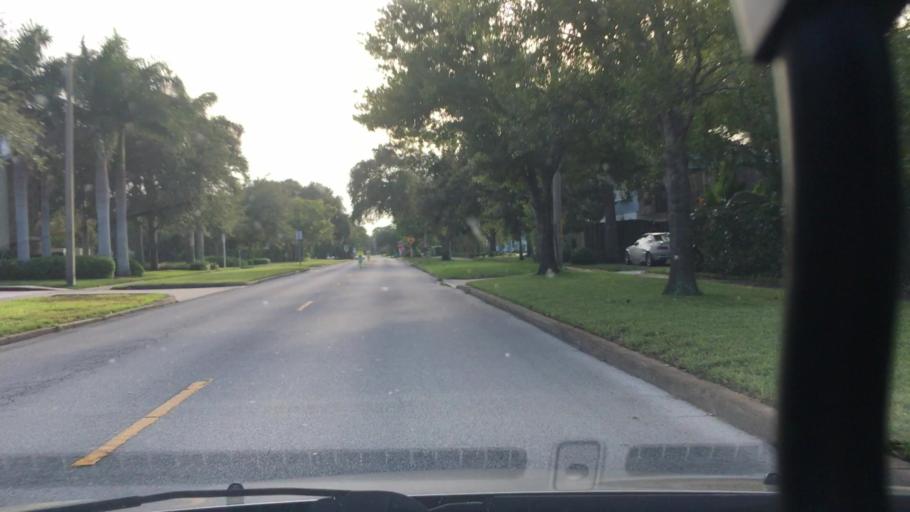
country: US
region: Florida
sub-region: Indian River County
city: Vero Beach
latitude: 27.6422
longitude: -80.4036
